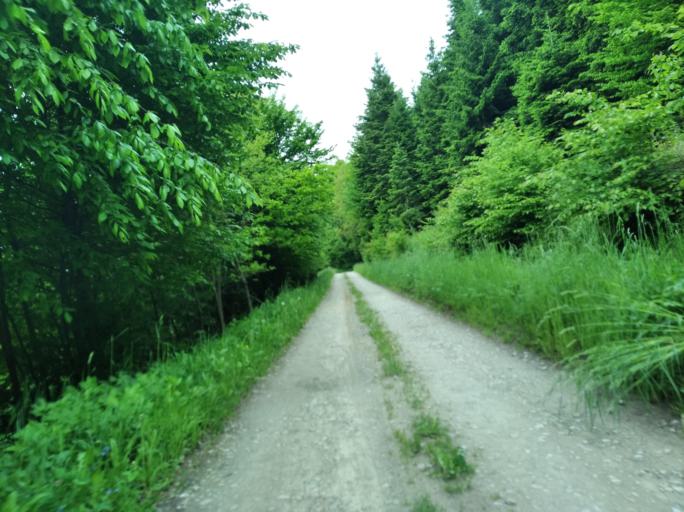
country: PL
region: Subcarpathian Voivodeship
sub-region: Powiat brzozowski
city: Jasionow
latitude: 49.6703
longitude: 21.9841
